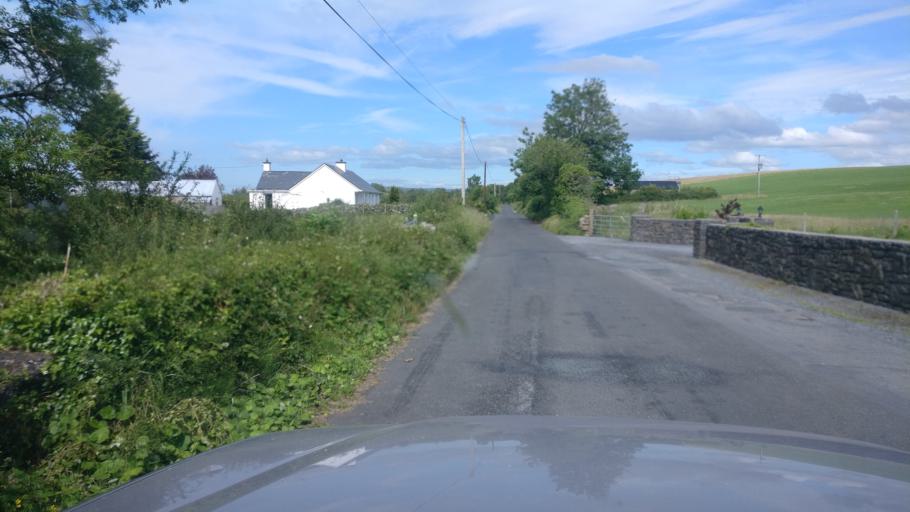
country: IE
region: Connaught
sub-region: County Galway
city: Gort
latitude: 53.0727
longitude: -8.7817
